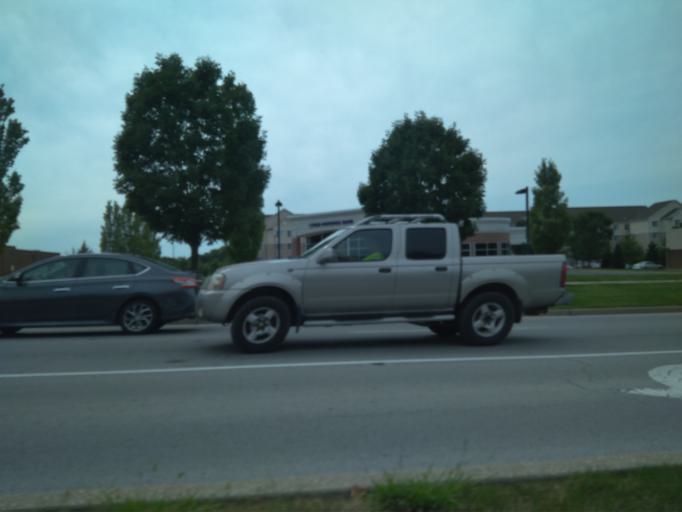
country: US
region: Kentucky
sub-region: Jefferson County
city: Hurstbourne
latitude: 38.2517
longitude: -85.5793
